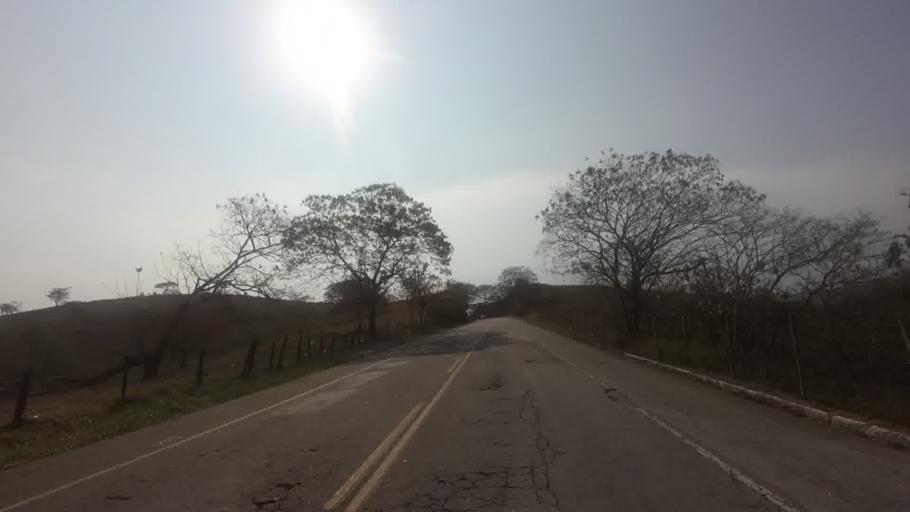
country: BR
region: Rio de Janeiro
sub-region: Bom Jesus Do Itabapoana
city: Bom Jesus do Itabapoana
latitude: -21.1393
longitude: -41.6316
